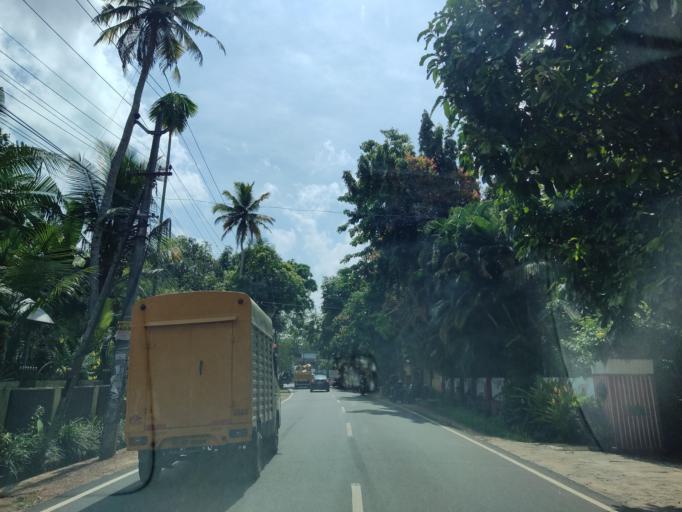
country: IN
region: Kerala
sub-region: Alappuzha
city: Mavelikara
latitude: 9.2715
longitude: 76.5374
